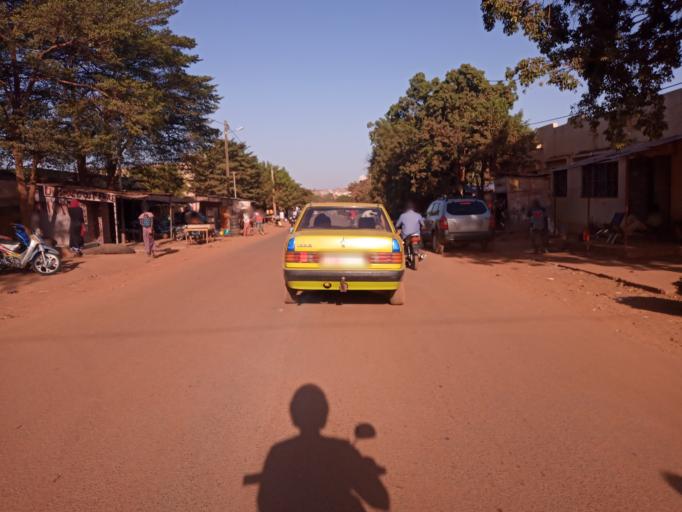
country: ML
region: Bamako
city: Bamako
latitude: 12.6125
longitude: -7.9533
